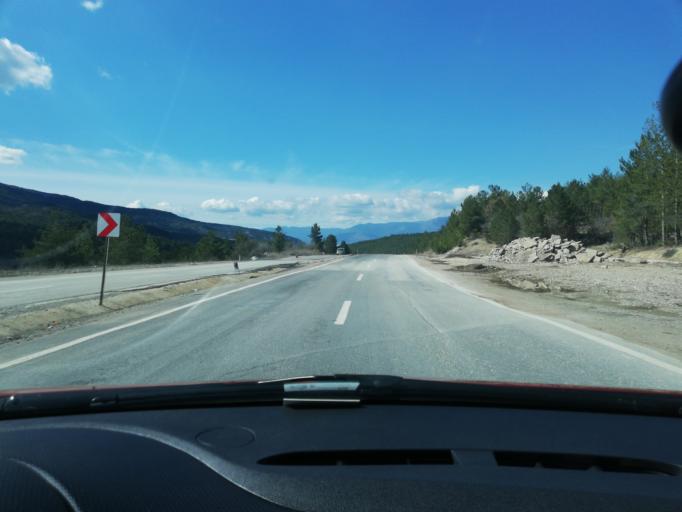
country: TR
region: Karabuk
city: Safranbolu
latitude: 41.1976
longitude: 32.8314
